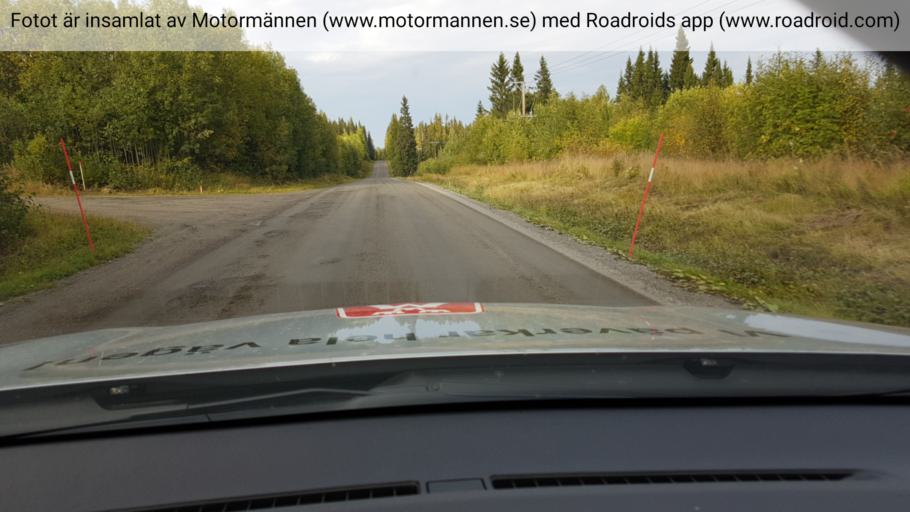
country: SE
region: Jaemtland
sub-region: Stroemsunds Kommun
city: Stroemsund
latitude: 63.9965
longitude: 15.8166
